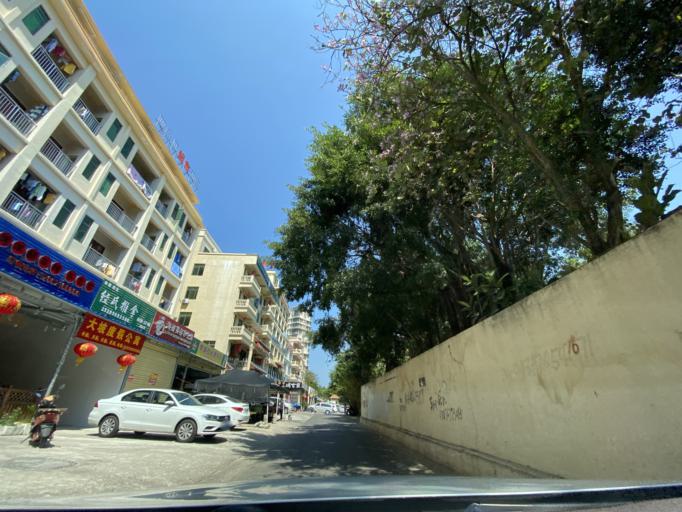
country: CN
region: Hainan
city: Yingzhou
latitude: 18.4041
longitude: 109.8454
